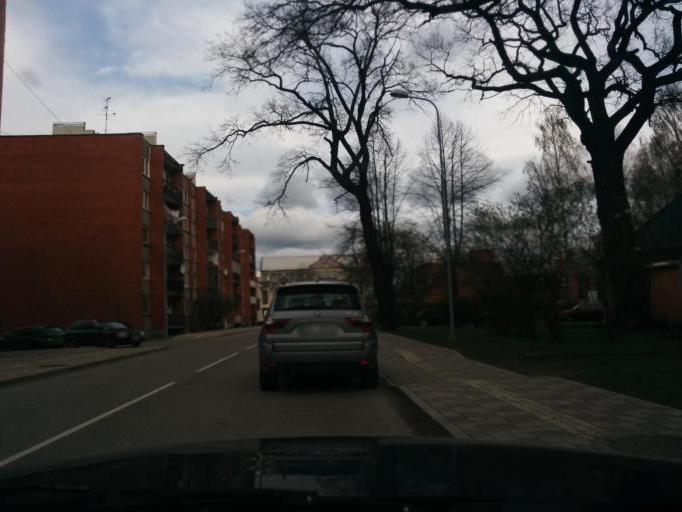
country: LV
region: Jelgava
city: Jelgava
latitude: 56.6447
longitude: 23.7283
